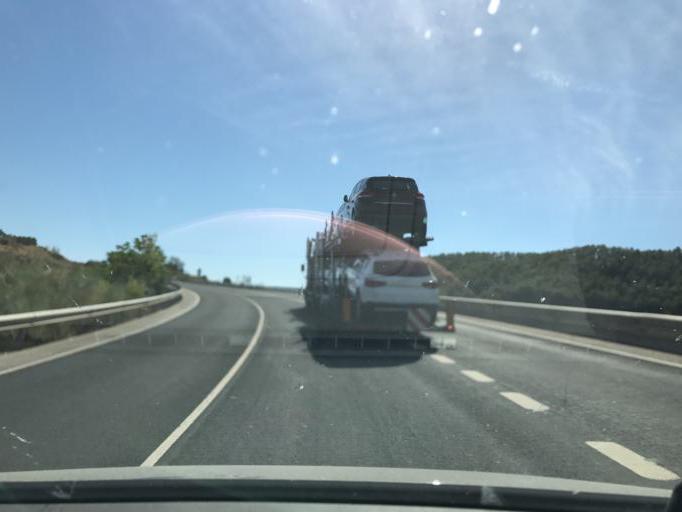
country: ES
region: Andalusia
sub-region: Province of Cordoba
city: Fuente-Tojar
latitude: 37.5761
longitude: -4.1577
